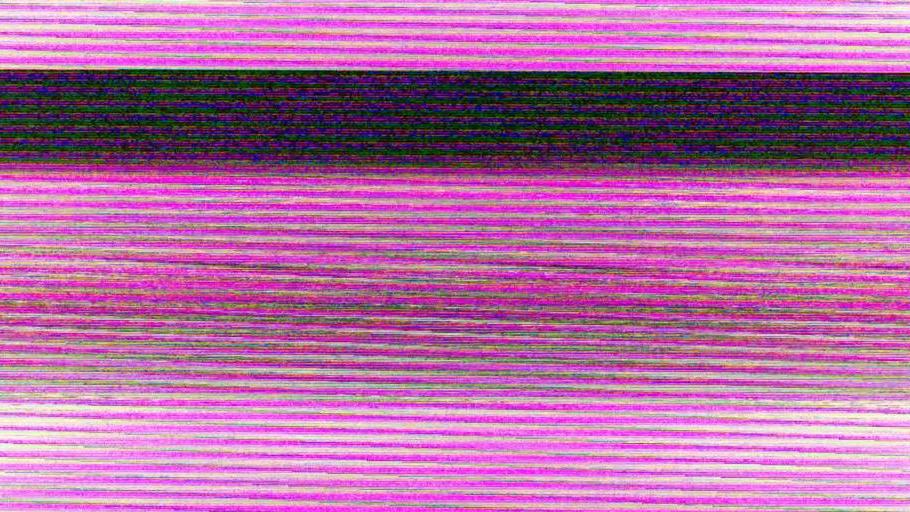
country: US
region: Massachusetts
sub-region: Middlesex County
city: Shirley
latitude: 42.5261
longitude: -71.6309
